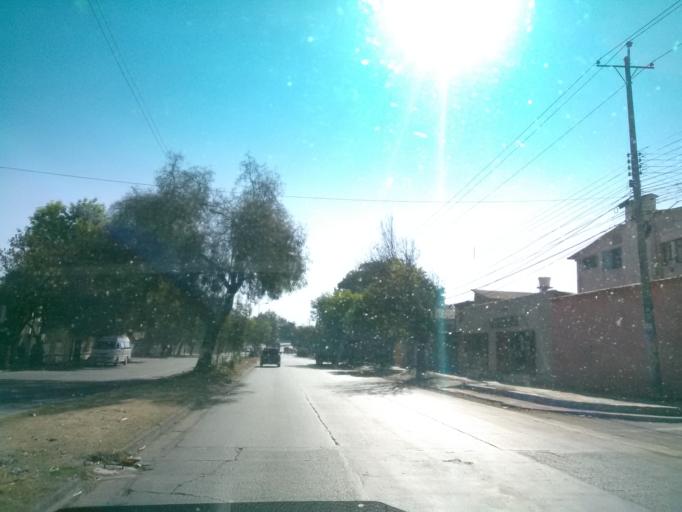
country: BO
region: Cochabamba
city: Cochabamba
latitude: -17.3638
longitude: -66.1659
